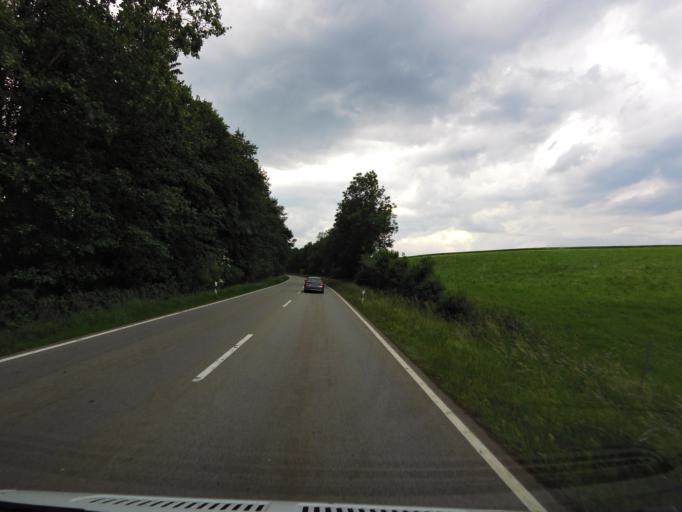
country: DE
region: Bavaria
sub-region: Lower Bavaria
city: Hutthurm
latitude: 48.6842
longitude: 13.4671
